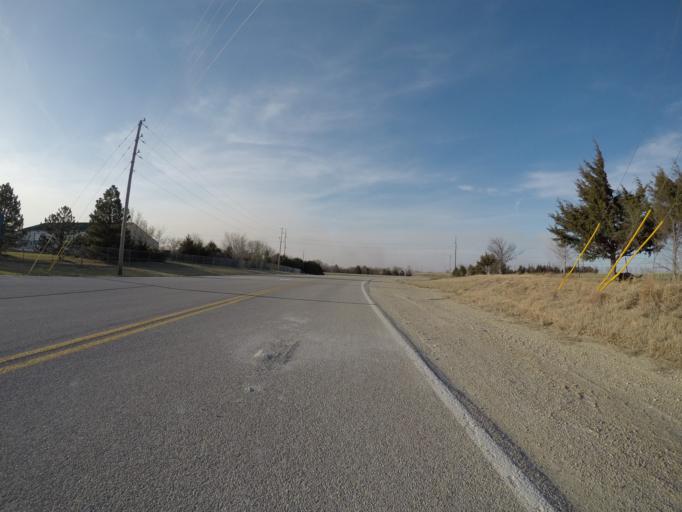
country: US
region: Kansas
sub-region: Riley County
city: Manhattan
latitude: 39.2502
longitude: -96.6538
